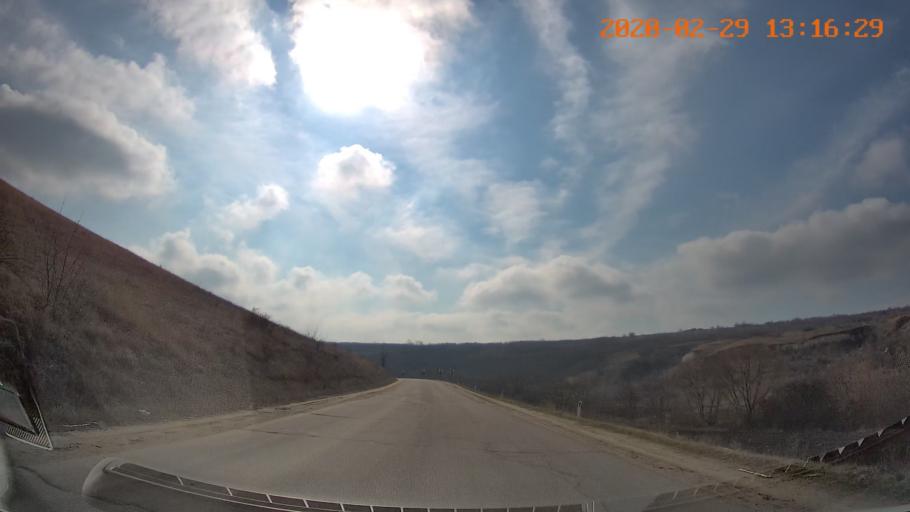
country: MD
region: Telenesti
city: Camenca
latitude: 48.0023
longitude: 28.6635
